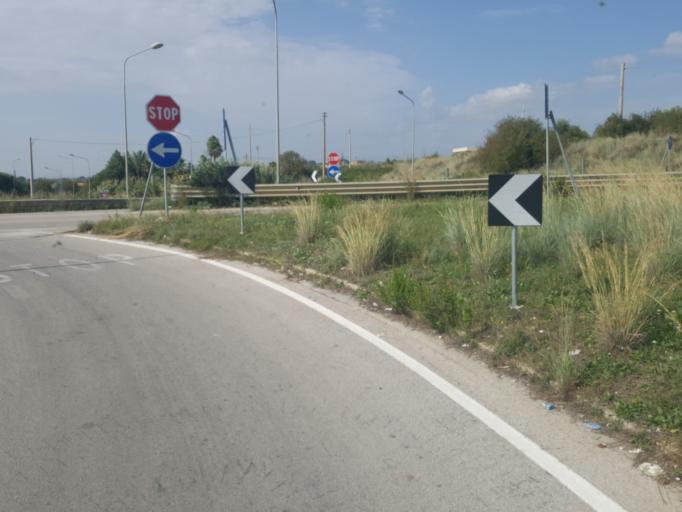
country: IT
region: Sicily
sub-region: Agrigento
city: Menfi
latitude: 37.6168
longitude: 12.9753
